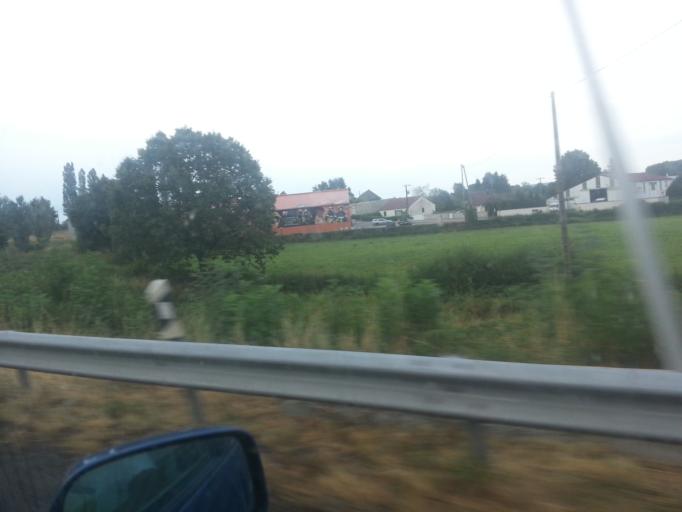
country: FR
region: Bourgogne
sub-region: Departement de Saone-et-Loire
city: Genelard
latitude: 46.5907
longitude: 4.2281
